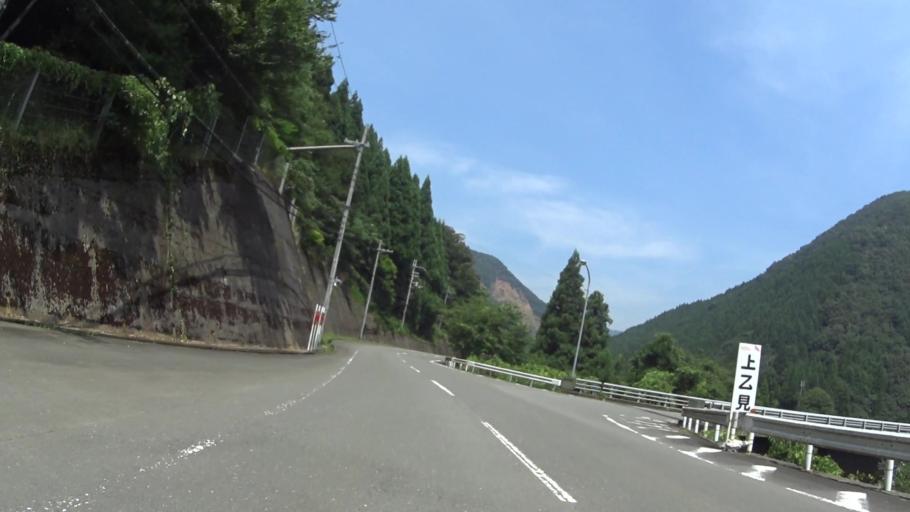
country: JP
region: Kyoto
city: Ayabe
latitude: 35.2815
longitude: 135.4297
